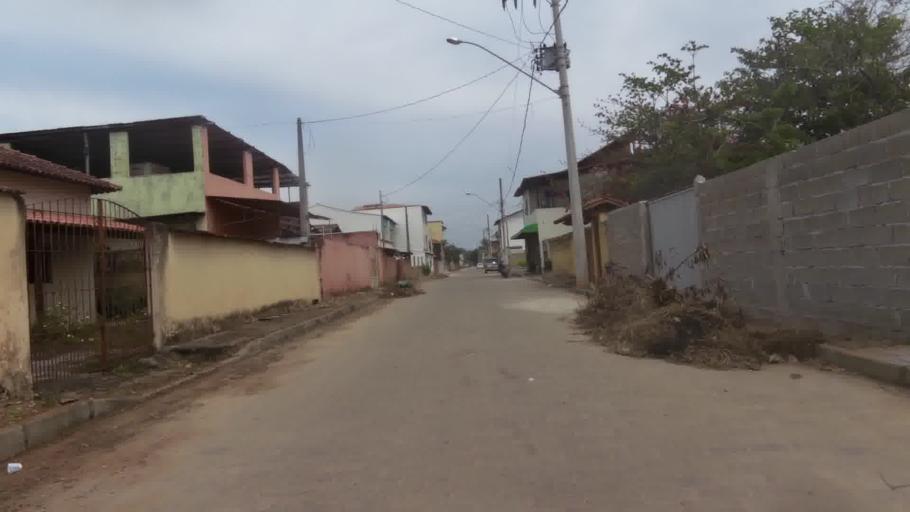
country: BR
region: Espirito Santo
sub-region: Piuma
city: Piuma
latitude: -20.8445
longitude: -40.7477
